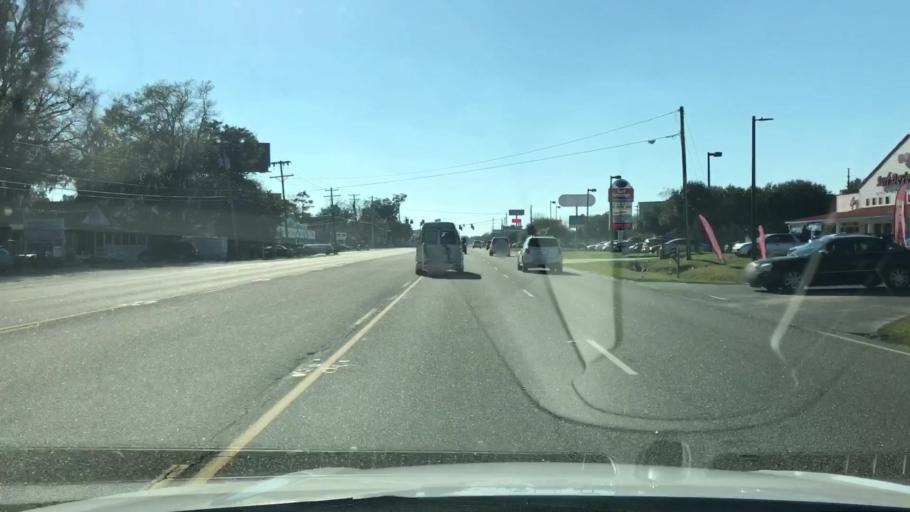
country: US
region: South Carolina
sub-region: Horry County
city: Garden City
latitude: 33.5805
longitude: -79.0199
